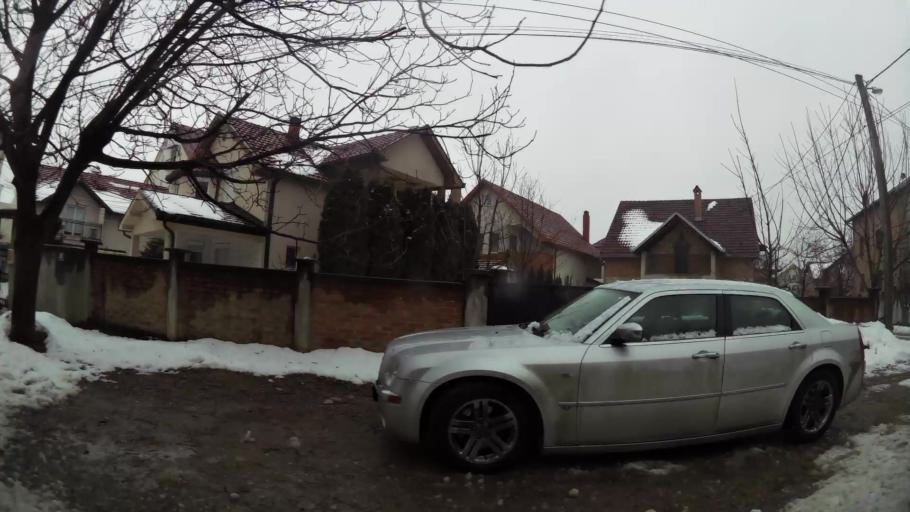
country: RS
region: Central Serbia
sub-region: Belgrade
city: Zemun
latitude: 44.8544
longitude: 20.3508
